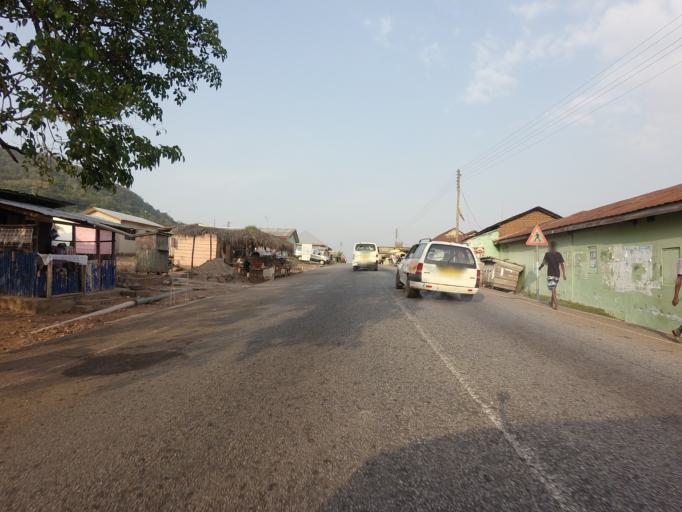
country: GH
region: Volta
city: Ho
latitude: 6.5379
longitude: 0.2850
